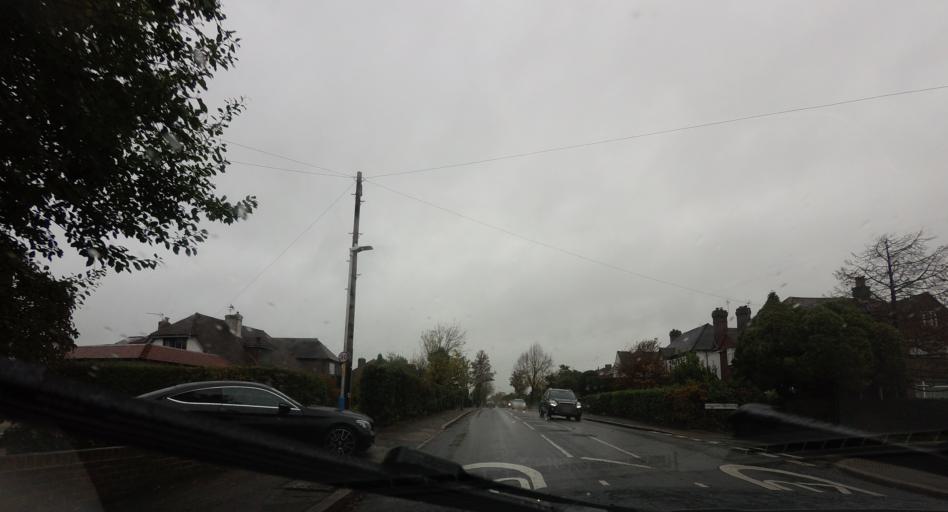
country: GB
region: England
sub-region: Kent
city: Tonbridge
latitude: 51.2049
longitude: 0.2864
